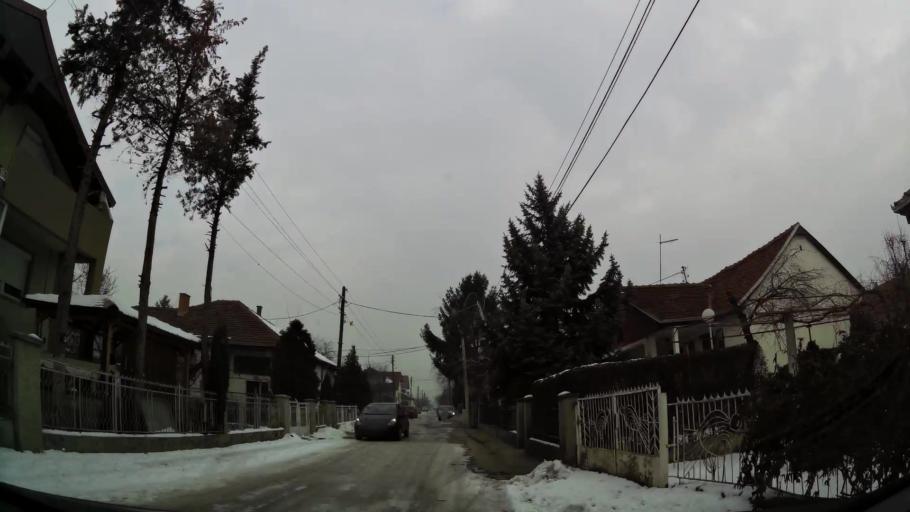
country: MK
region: Saraj
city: Saraj
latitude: 42.0186
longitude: 21.3600
